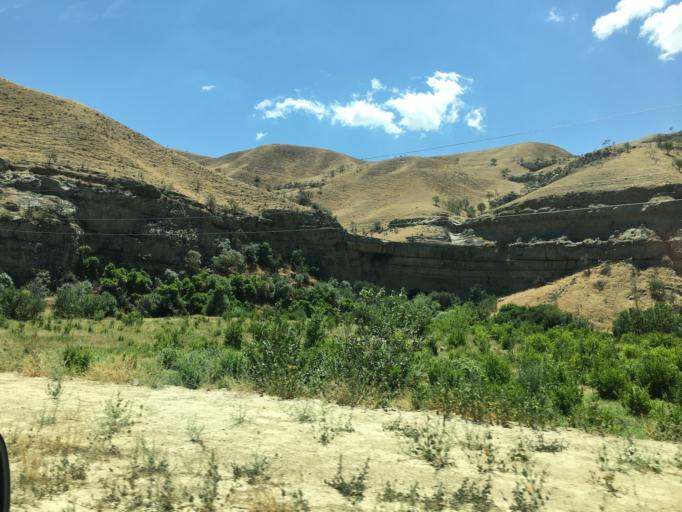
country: TM
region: Balkan
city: Magtymguly
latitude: 38.4210
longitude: 56.6526
